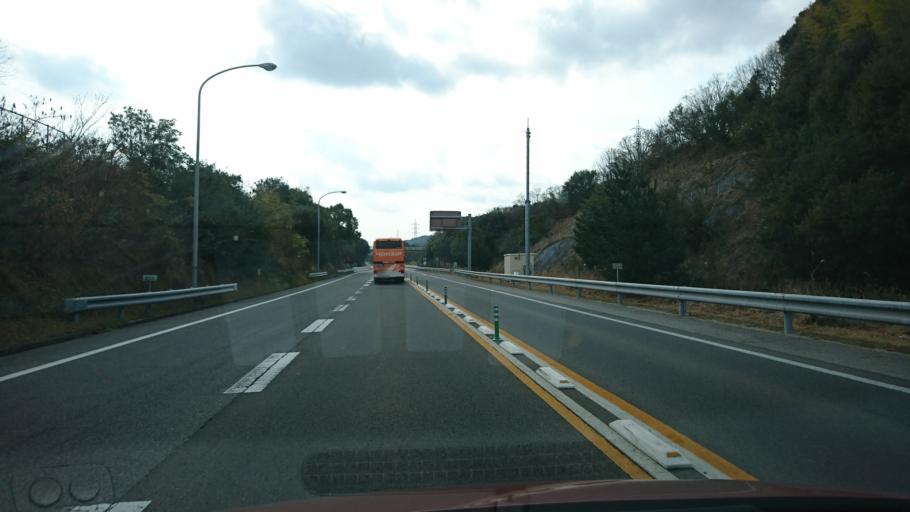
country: JP
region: Hiroshima
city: Innoshima
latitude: 34.2469
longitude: 133.0481
